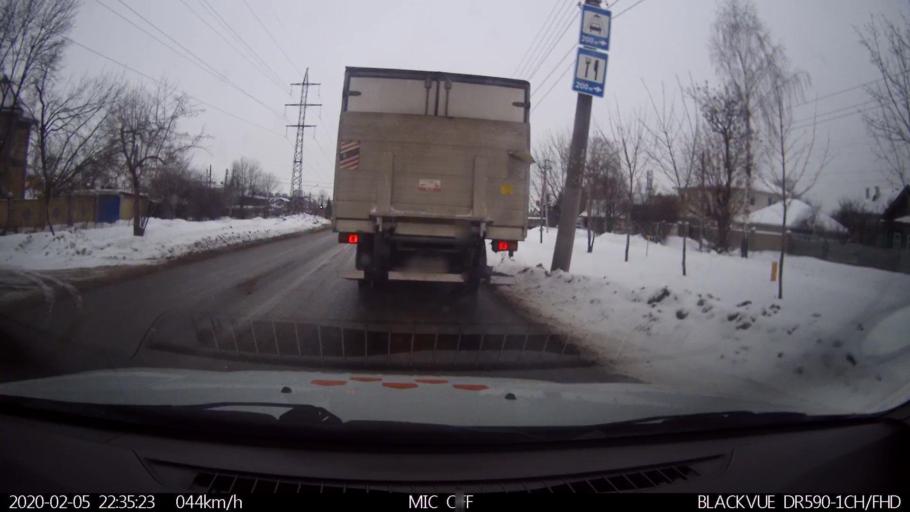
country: RU
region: Nizjnij Novgorod
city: Imeni Stepana Razina
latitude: 54.7345
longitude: 44.2402
